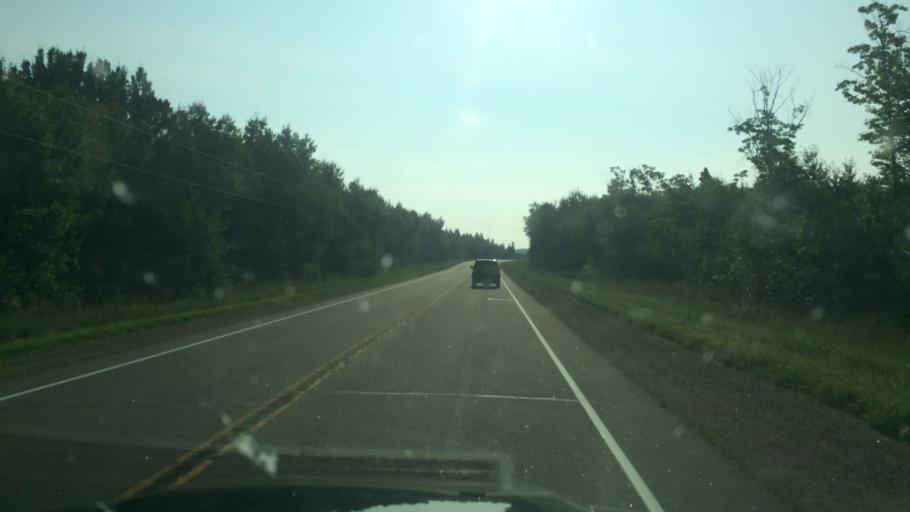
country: US
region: Wisconsin
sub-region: Lincoln County
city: Merrill
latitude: 45.1482
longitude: -89.4214
